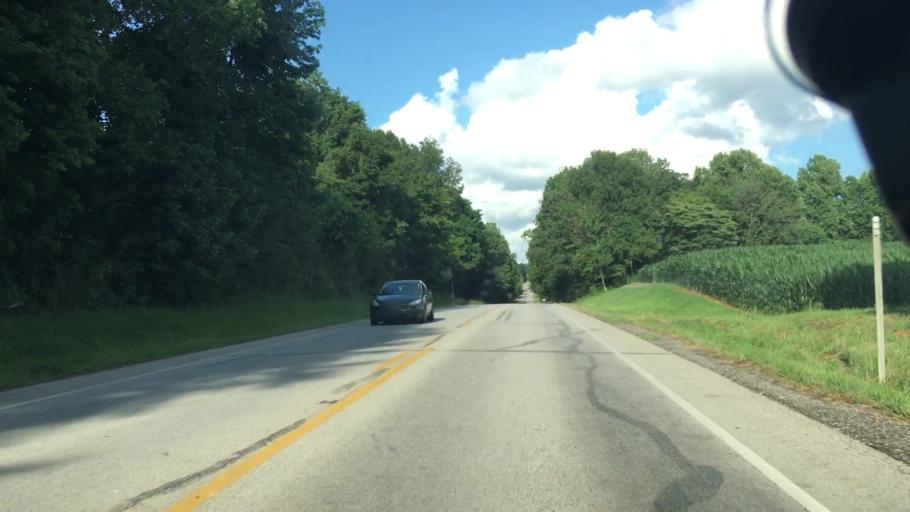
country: US
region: Kentucky
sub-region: Hancock County
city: Lewisport
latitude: 38.0014
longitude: -86.8456
